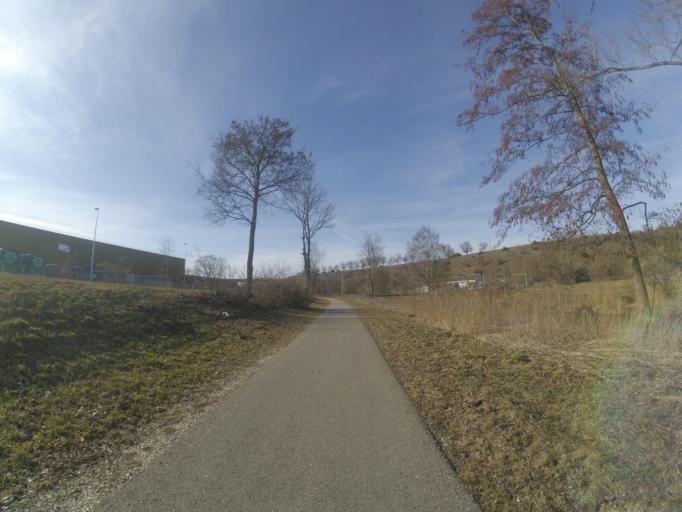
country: DE
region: Baden-Wuerttemberg
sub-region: Regierungsbezirk Stuttgart
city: Giengen an der Brenz
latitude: 48.6255
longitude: 10.2297
